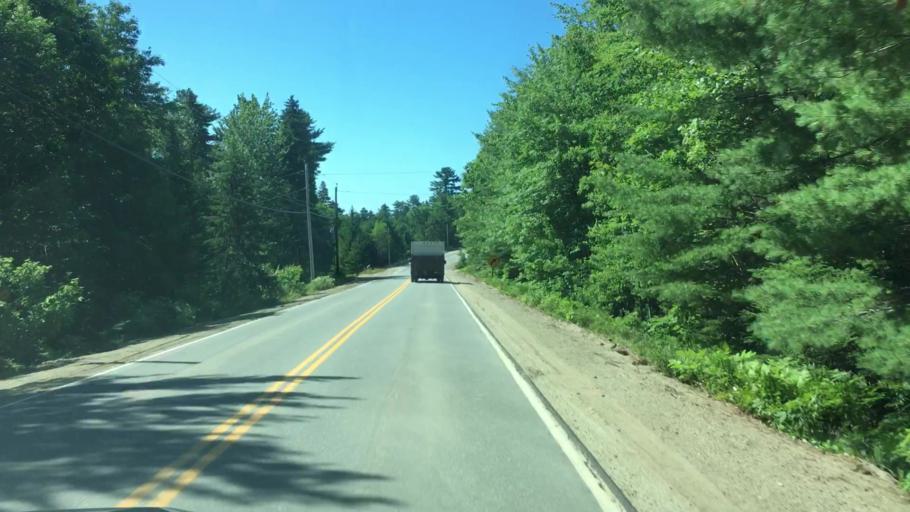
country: US
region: Maine
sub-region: Hancock County
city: Sedgwick
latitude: 44.3703
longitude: -68.5673
